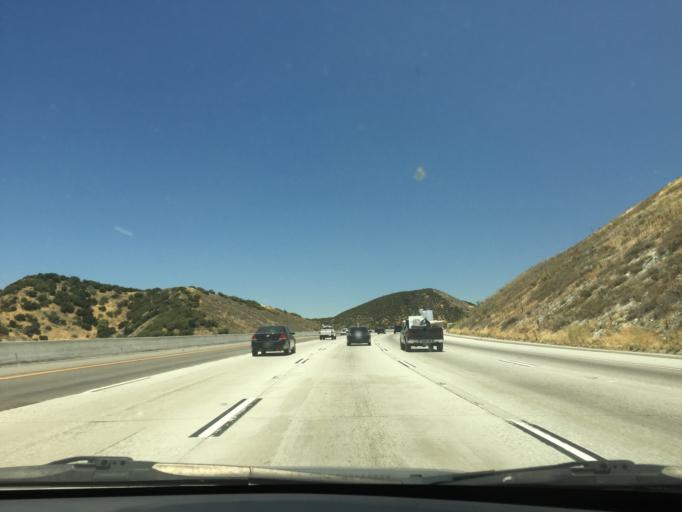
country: US
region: California
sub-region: San Bernardino County
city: Oak Hills
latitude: 34.2548
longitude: -117.4490
